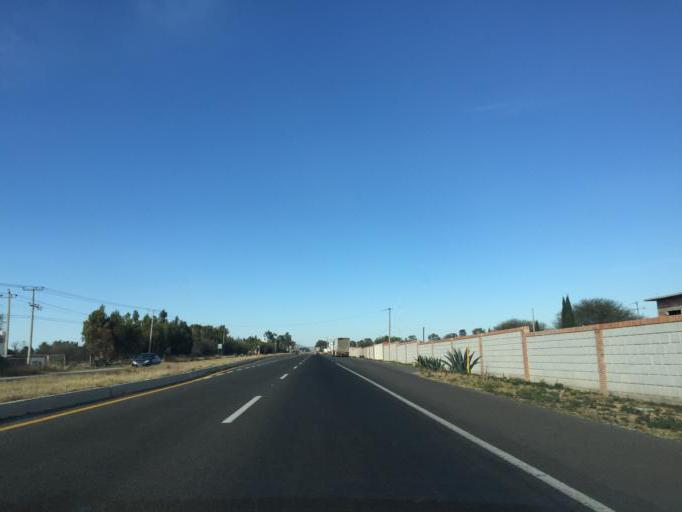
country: MX
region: Queretaro
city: Ezequiel Montes
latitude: 20.6199
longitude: -99.9138
